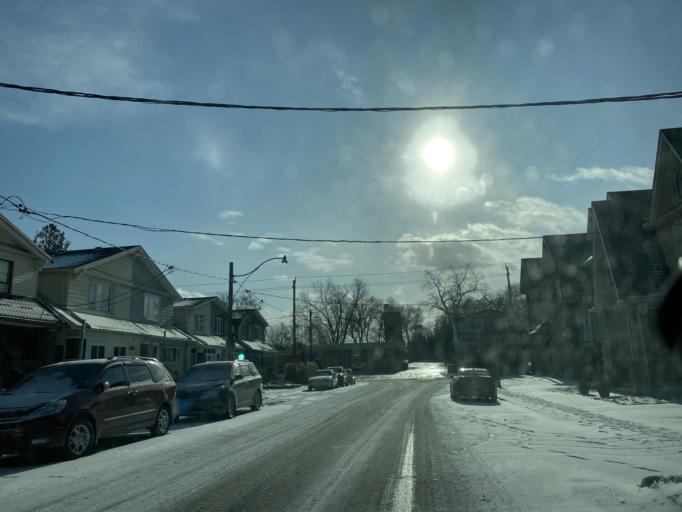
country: CA
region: Ontario
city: Toronto
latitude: 43.6804
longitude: -79.3352
